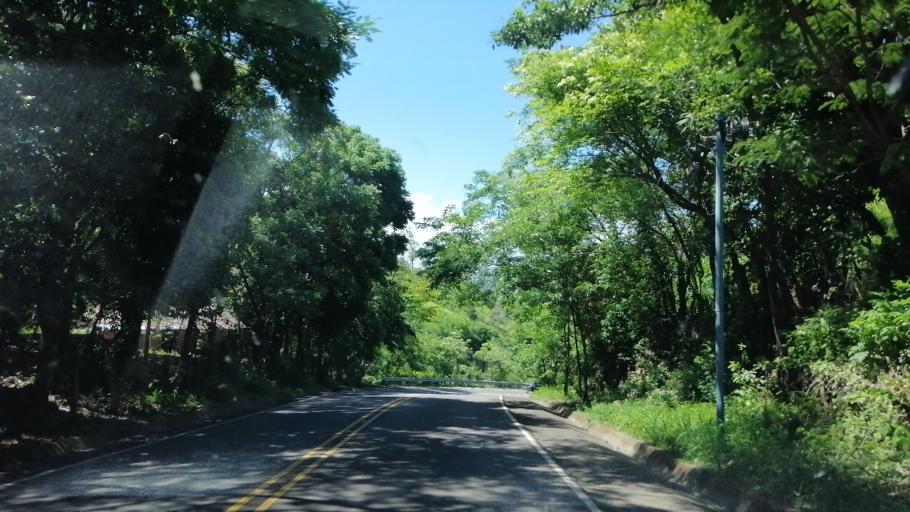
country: SV
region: San Miguel
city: Ciudad Barrios
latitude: 13.8147
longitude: -88.1870
